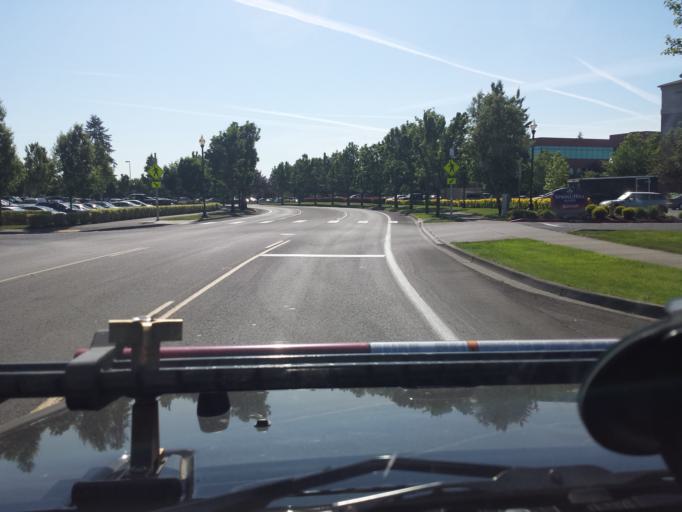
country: US
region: Washington
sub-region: Clark County
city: Mill Plain
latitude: 45.6121
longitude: -122.5026
